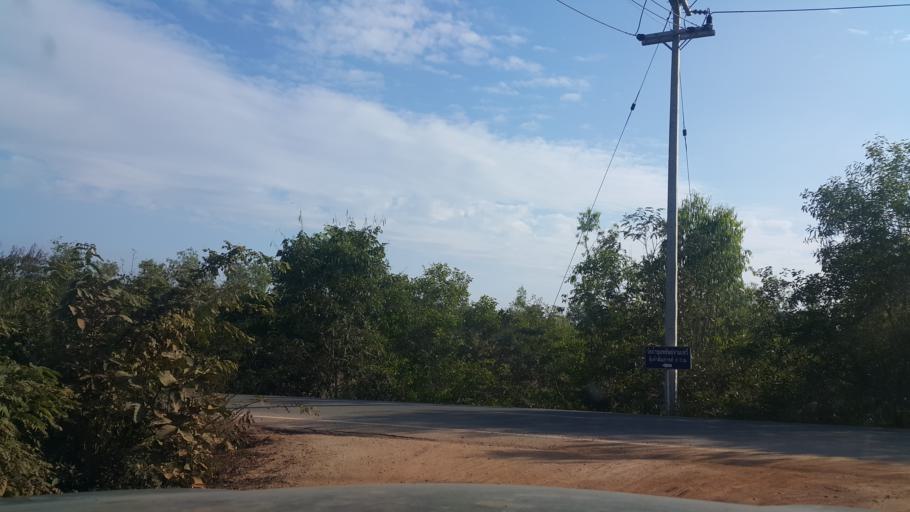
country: TH
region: Lampang
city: Hang Chat
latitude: 18.3000
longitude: 99.3528
